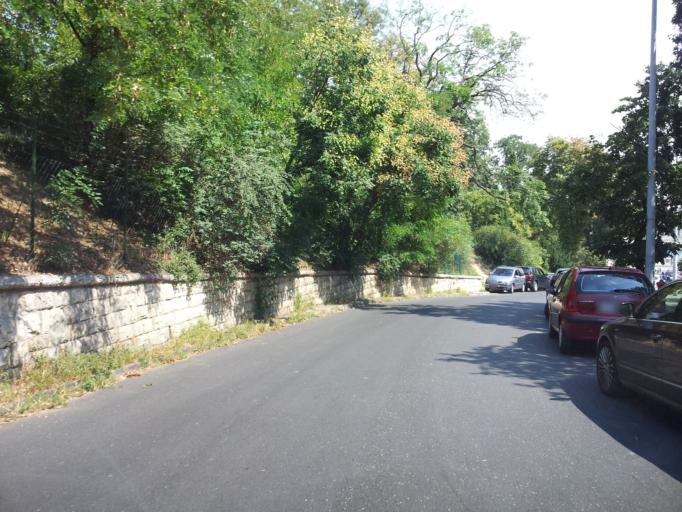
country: HU
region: Budapest
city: Budapest IX. keruelet
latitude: 47.4839
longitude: 19.0503
